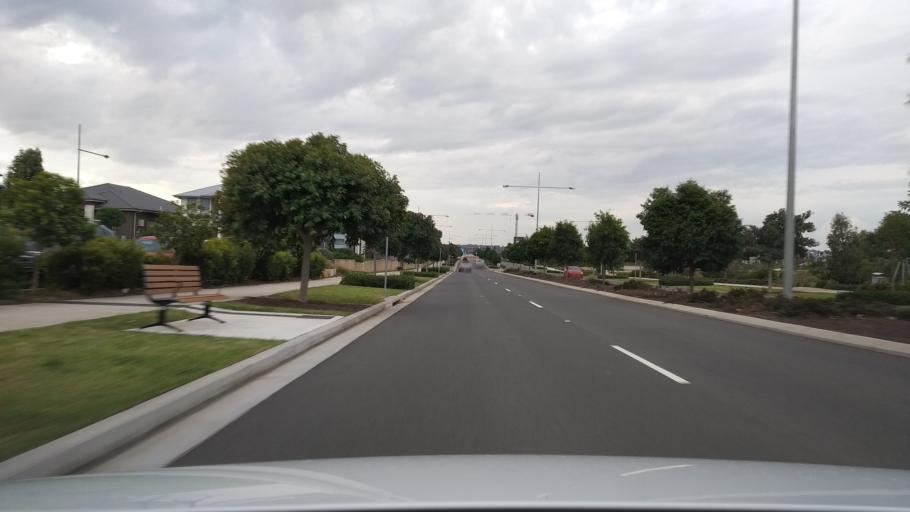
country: AU
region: New South Wales
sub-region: Camden
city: Narellan
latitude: -34.0035
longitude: 150.7316
